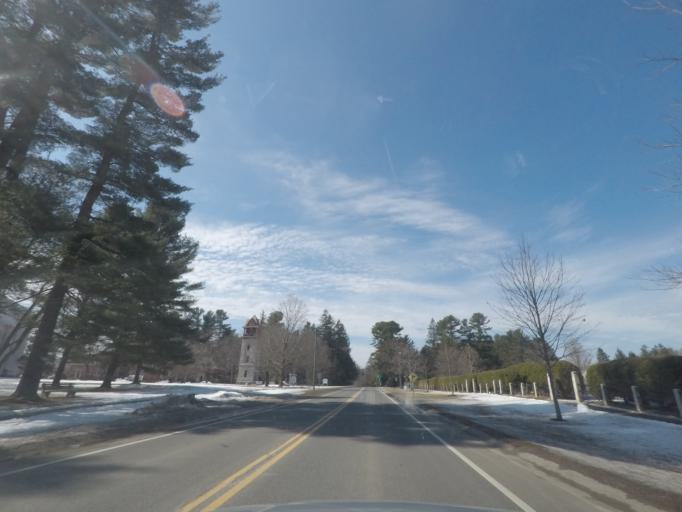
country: US
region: Massachusetts
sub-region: Berkshire County
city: Stockbridge
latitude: 42.2836
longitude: -73.3185
